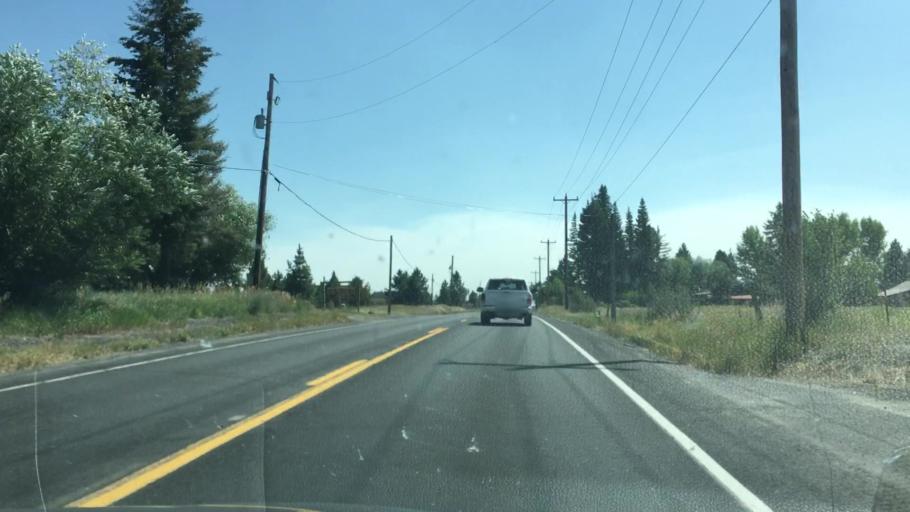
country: US
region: Idaho
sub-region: Valley County
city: McCall
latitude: 44.8722
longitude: -116.0908
